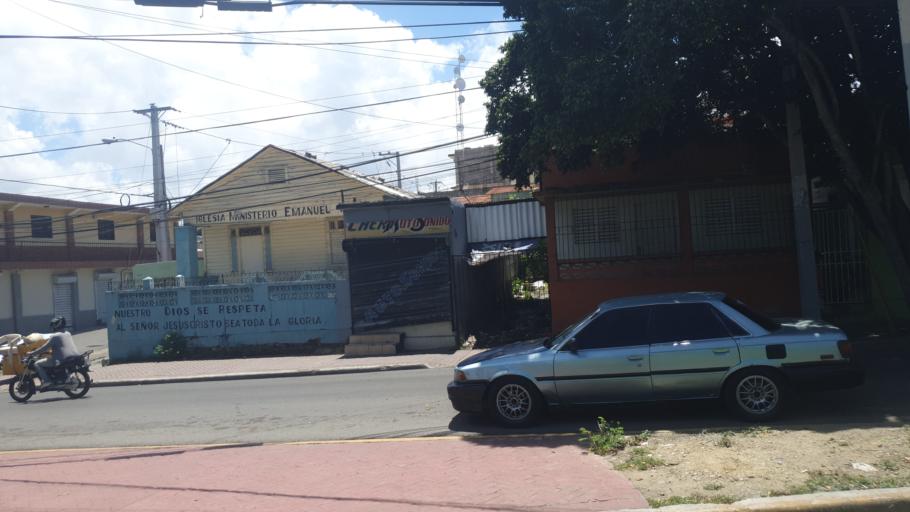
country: DO
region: Santiago
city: Santiago de los Caballeros
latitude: 19.4345
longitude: -70.6965
